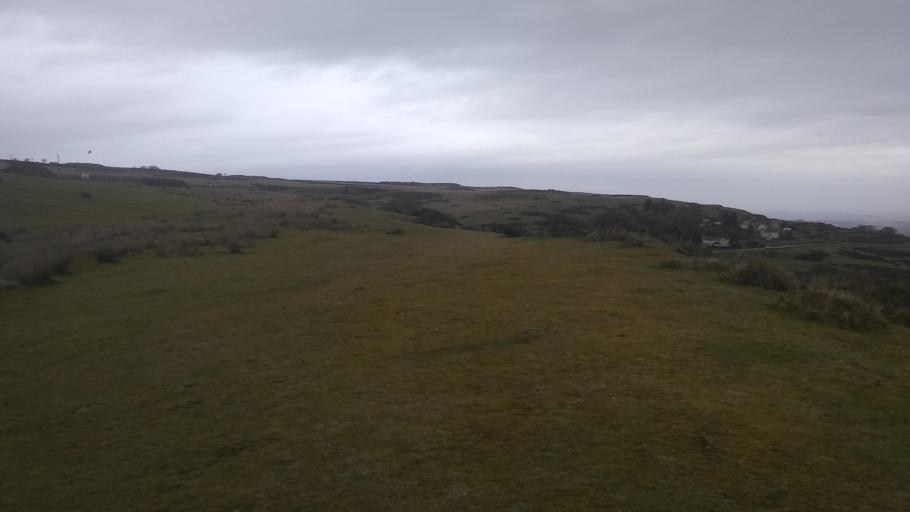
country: GB
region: England
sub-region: Worcestershire
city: Tenbury Wells
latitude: 52.3770
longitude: -2.5916
